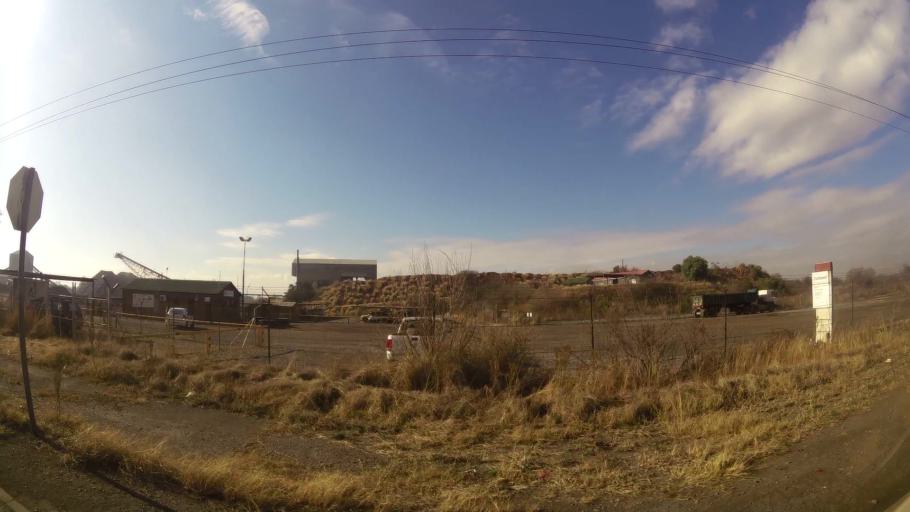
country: ZA
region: Gauteng
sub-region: Sedibeng District Municipality
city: Meyerton
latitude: -26.5120
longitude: 28.0530
